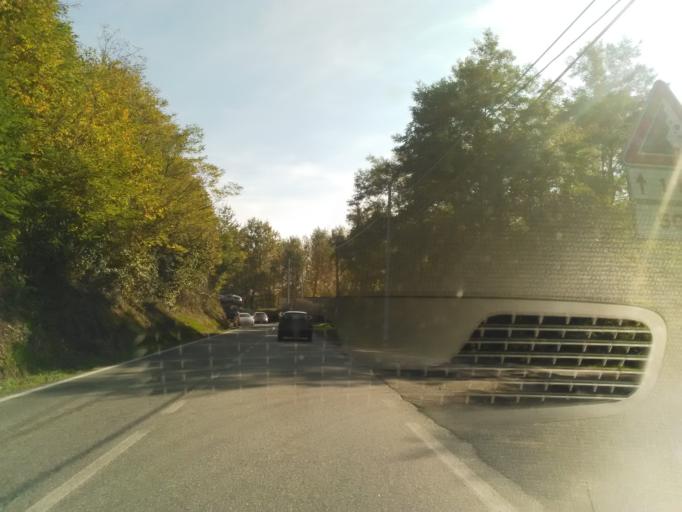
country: IT
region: Piedmont
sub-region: Provincia di Vercelli
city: Borgosesia
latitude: 45.6992
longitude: 8.2745
